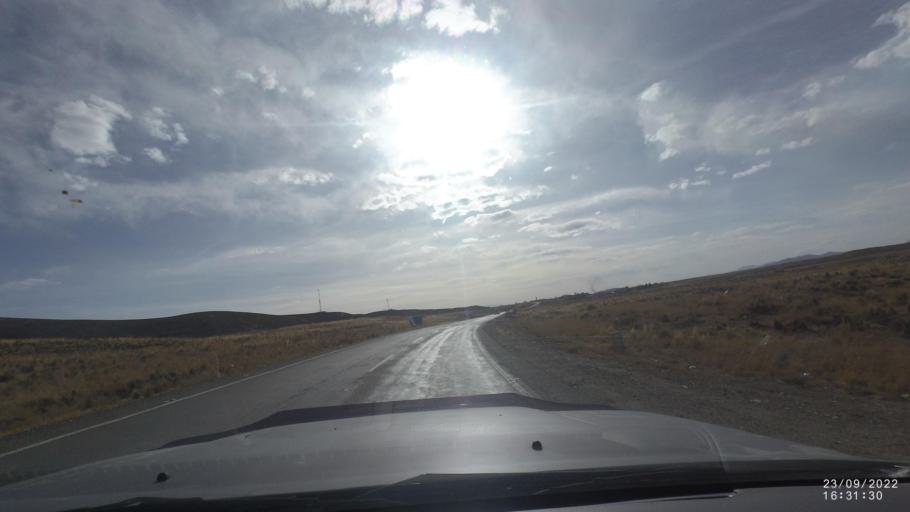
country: BO
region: Oruro
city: Machacamarca
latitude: -18.1666
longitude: -66.9918
